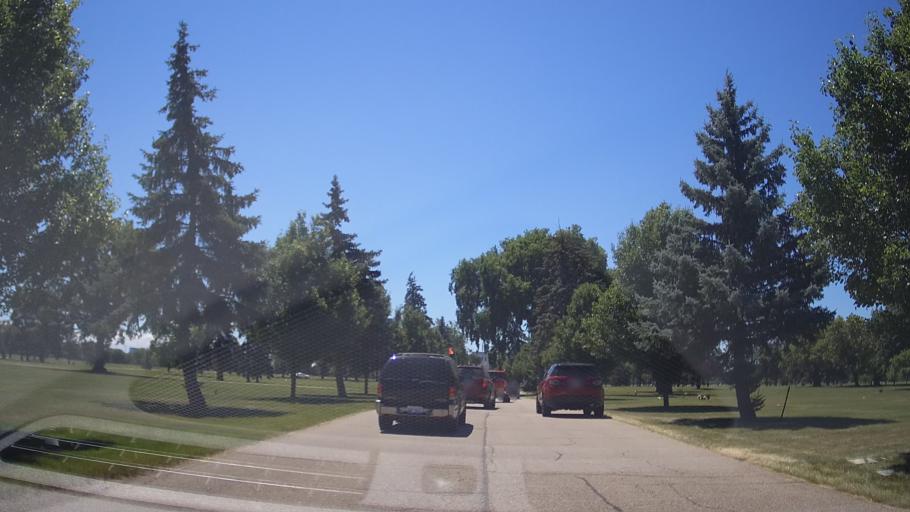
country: US
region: Michigan
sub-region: Oakland County
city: Troy
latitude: 42.5898
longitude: -83.1637
